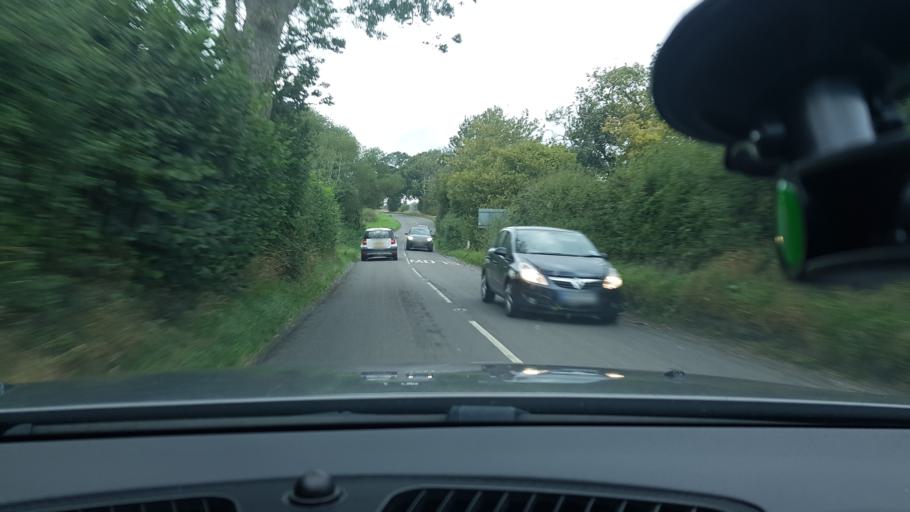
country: GB
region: England
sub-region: Wiltshire
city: Great Bedwyn
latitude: 51.3431
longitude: -1.6032
